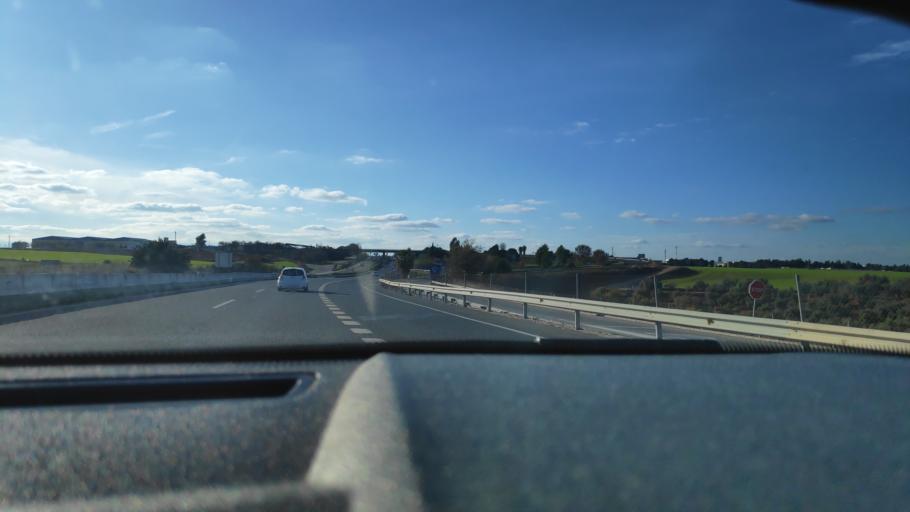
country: ES
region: Andalusia
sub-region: Provincia de Sevilla
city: Ecija
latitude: 37.5264
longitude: -5.1066
